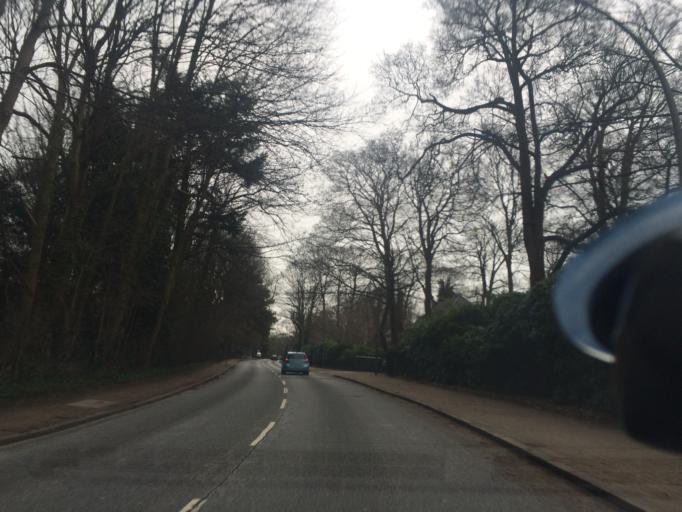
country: DE
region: Hamburg
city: Altona
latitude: 53.5469
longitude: 9.8754
